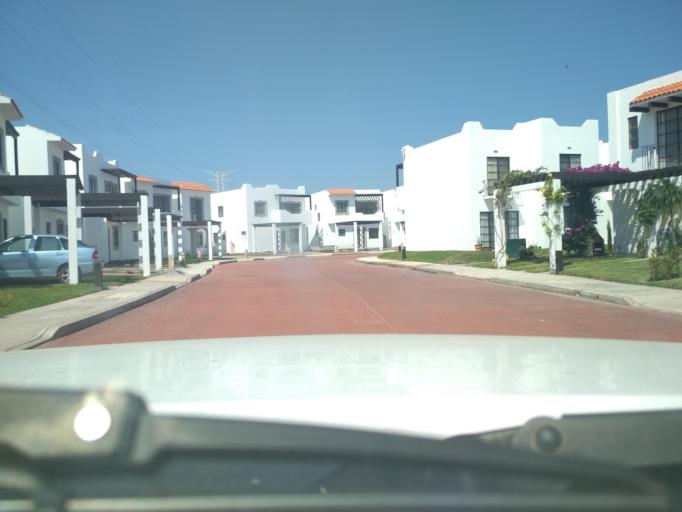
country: MX
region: Veracruz
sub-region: Veracruz
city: Lomas de Rio Medio Cuatro
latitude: 19.1799
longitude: -96.1928
